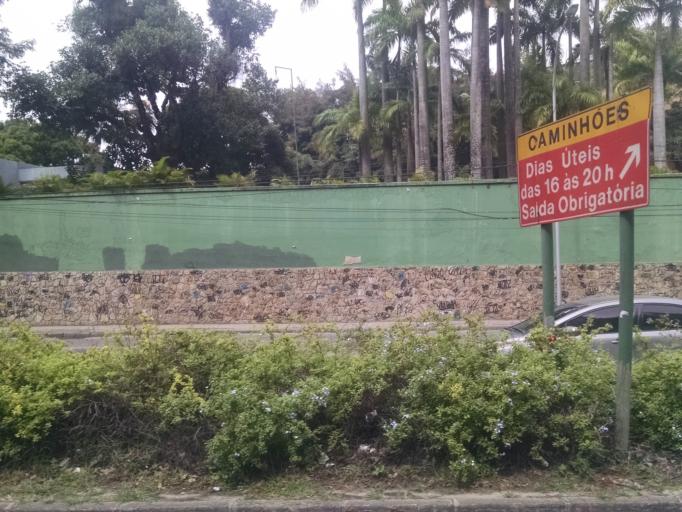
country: BR
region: Rio de Janeiro
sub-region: Rio De Janeiro
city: Rio de Janeiro
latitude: -22.9786
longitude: -43.2274
